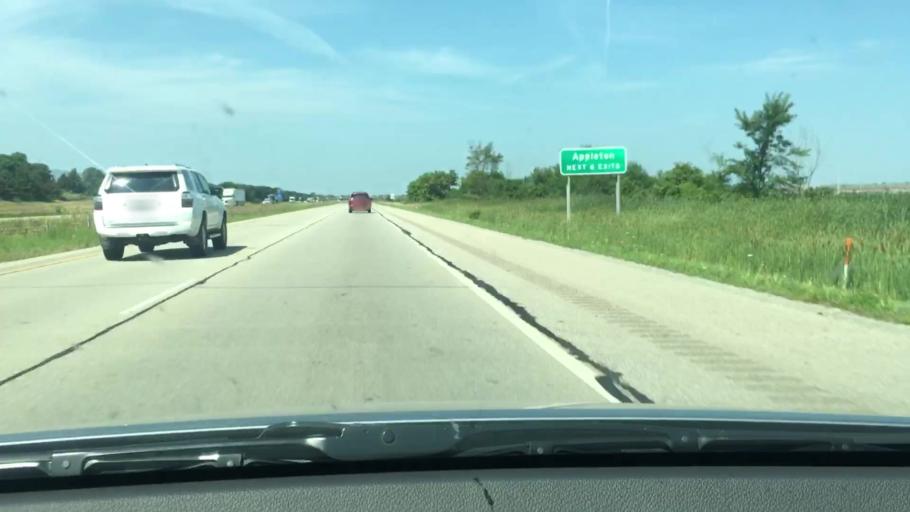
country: US
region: Wisconsin
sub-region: Outagamie County
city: Little Chute
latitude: 44.2981
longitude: -88.3352
